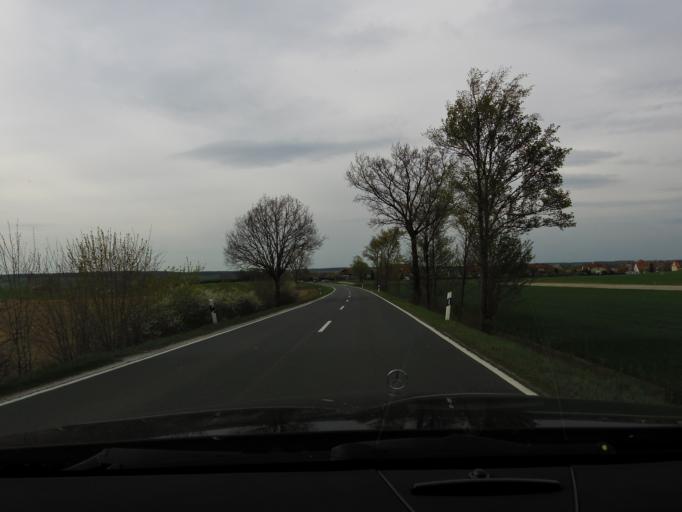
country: DE
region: Bavaria
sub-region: Upper Franconia
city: Pommersfelden
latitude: 49.7474
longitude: 10.8150
